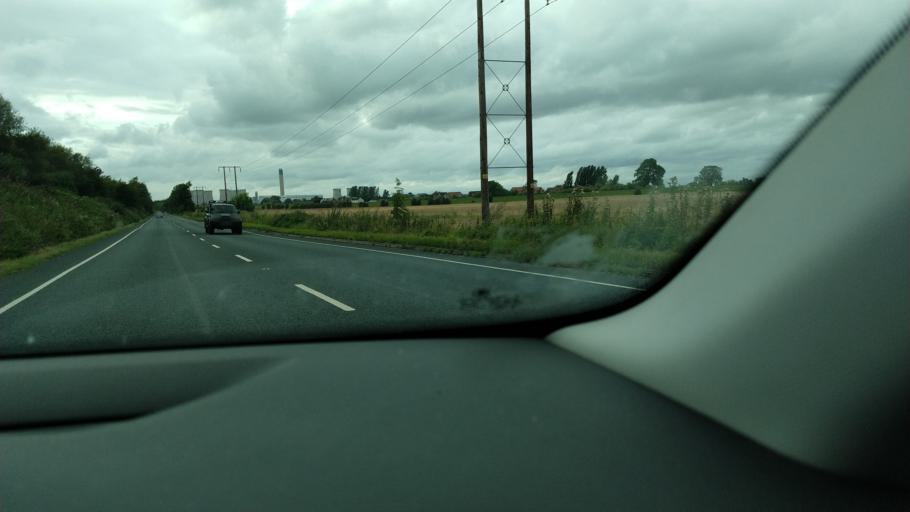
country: GB
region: England
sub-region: East Riding of Yorkshire
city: Rawcliffe
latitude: 53.7086
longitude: -0.9420
